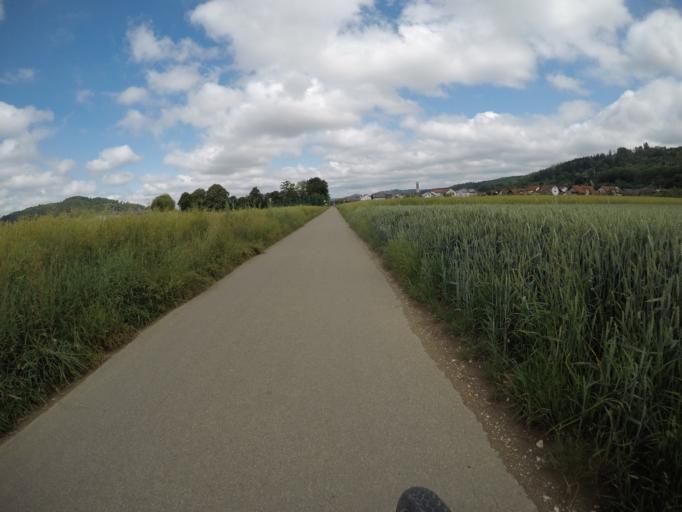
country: DE
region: Baden-Wuerttemberg
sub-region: Regierungsbezirk Stuttgart
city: Gingen an der Fils
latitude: 48.6522
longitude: 9.7900
